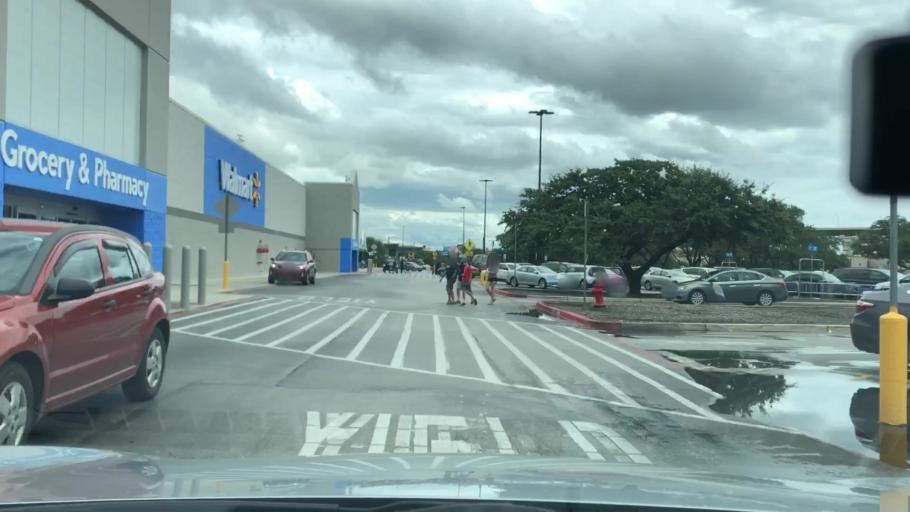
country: US
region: Texas
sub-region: Bexar County
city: Hollywood Park
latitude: 29.6119
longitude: -98.4716
